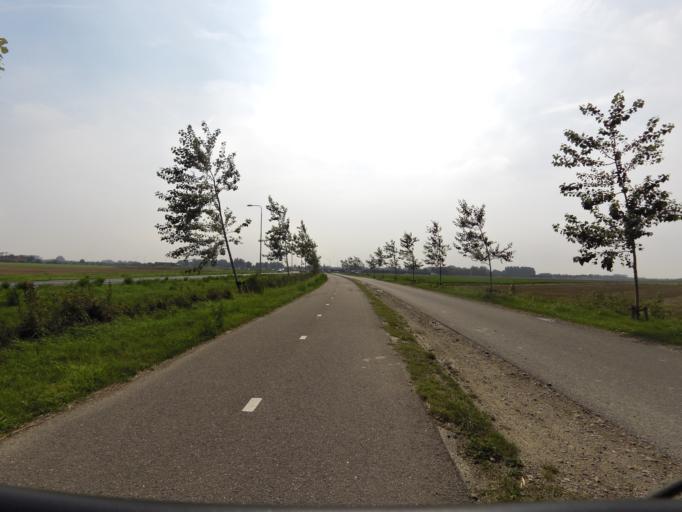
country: NL
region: Zeeland
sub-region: Gemeente Middelburg
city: Middelburg
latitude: 51.5600
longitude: 3.6002
